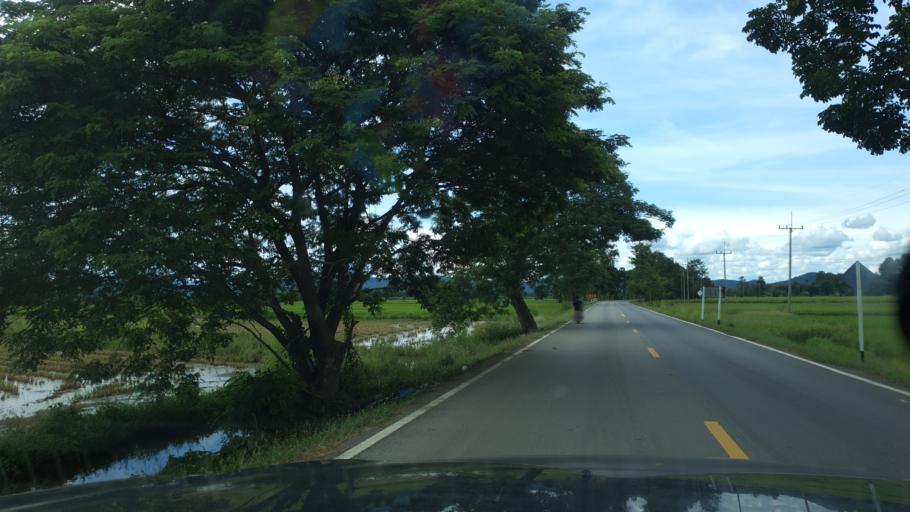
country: TH
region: Sukhothai
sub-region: Amphoe Si Satchanalai
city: Si Satchanalai
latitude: 17.4676
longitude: 99.7565
